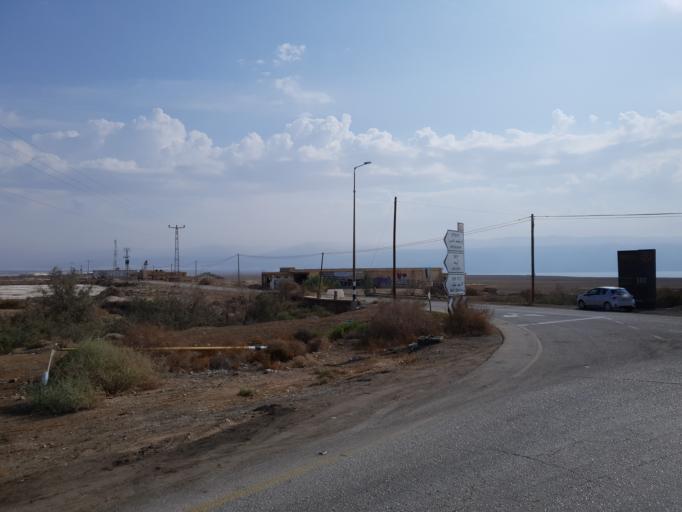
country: PS
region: West Bank
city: Jericho
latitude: 31.7736
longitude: 35.5053
